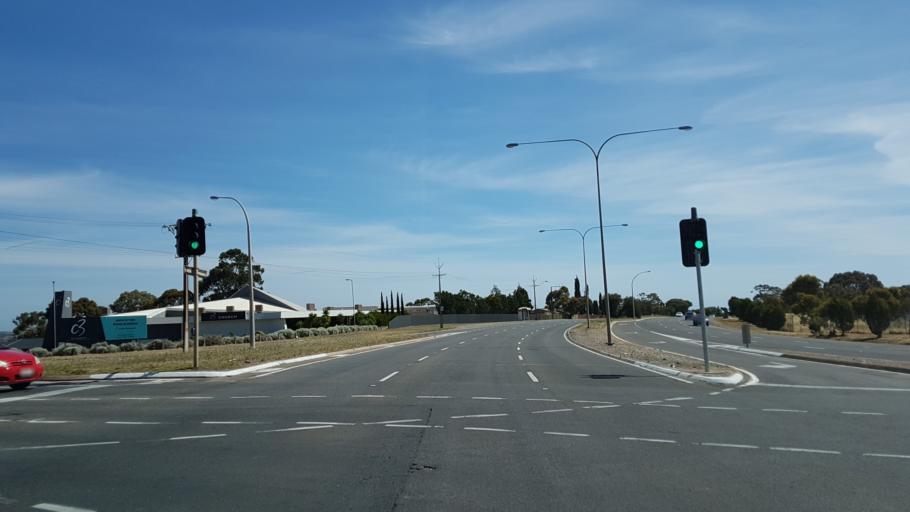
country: AU
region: South Australia
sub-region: Marion
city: Trott Park
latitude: -35.0605
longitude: 138.5595
